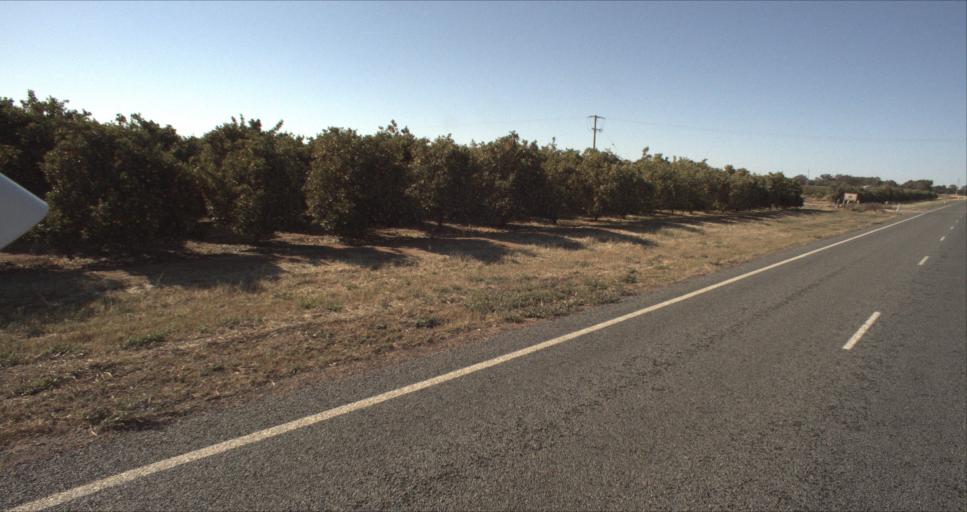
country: AU
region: New South Wales
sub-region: Leeton
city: Leeton
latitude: -34.6179
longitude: 146.3994
